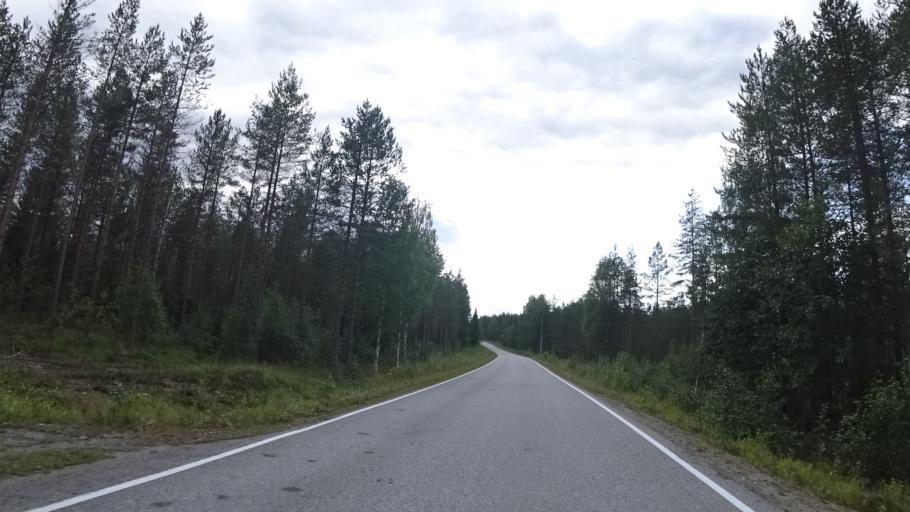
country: FI
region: North Karelia
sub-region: Joensuu
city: Ilomantsi
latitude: 62.4354
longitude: 31.0604
